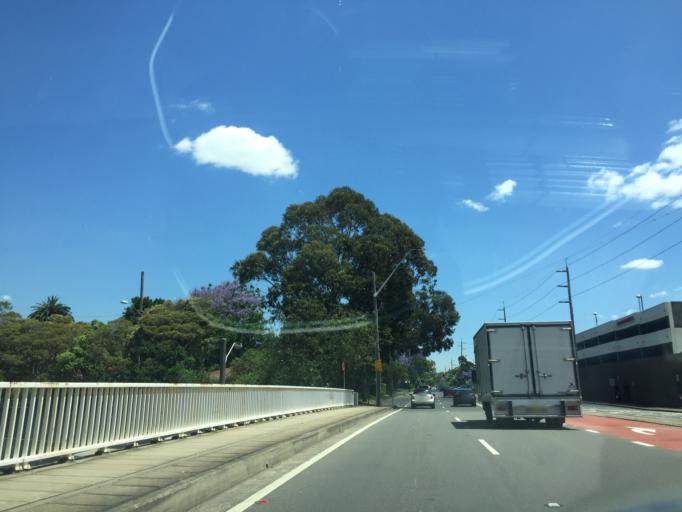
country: AU
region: New South Wales
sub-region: Ryde
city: Denistone
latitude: -33.7924
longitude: 151.0829
